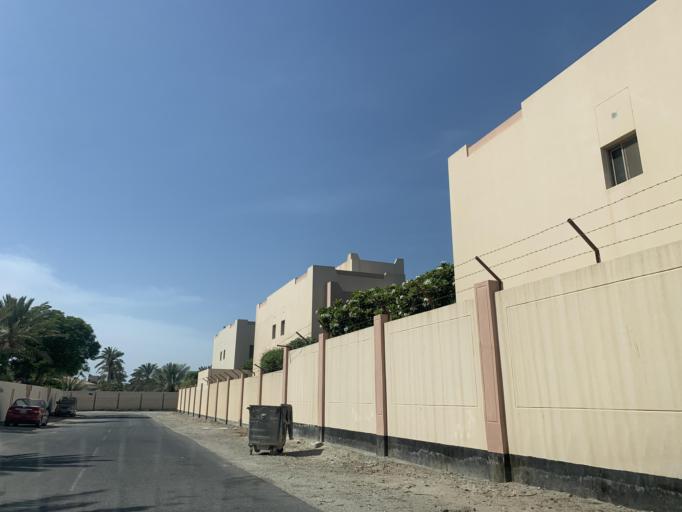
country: BH
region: Northern
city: Madinat `Isa
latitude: 26.1896
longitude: 50.4726
